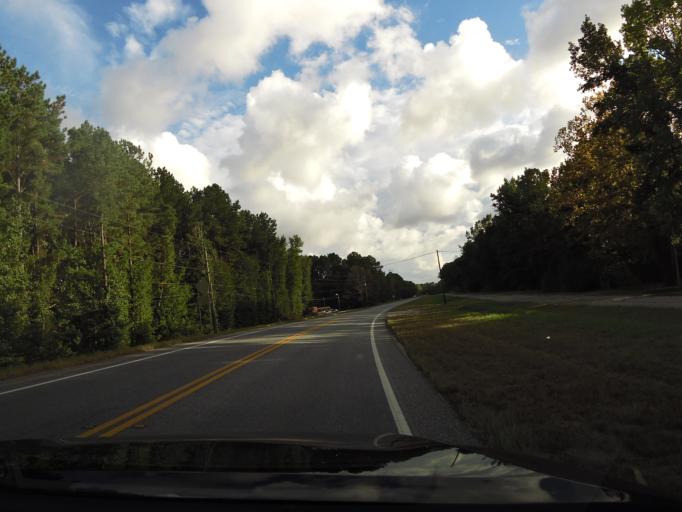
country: US
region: Georgia
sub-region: Liberty County
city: Midway
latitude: 31.7191
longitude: -81.4166
